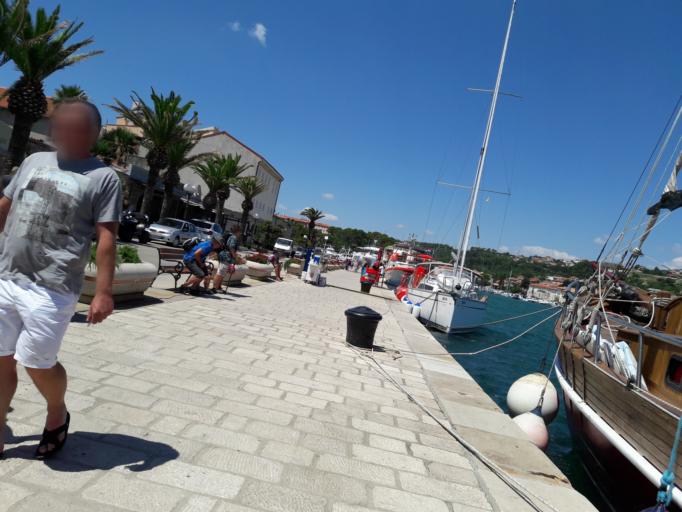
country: HR
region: Primorsko-Goranska
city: Banjol
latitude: 44.7562
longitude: 14.7618
